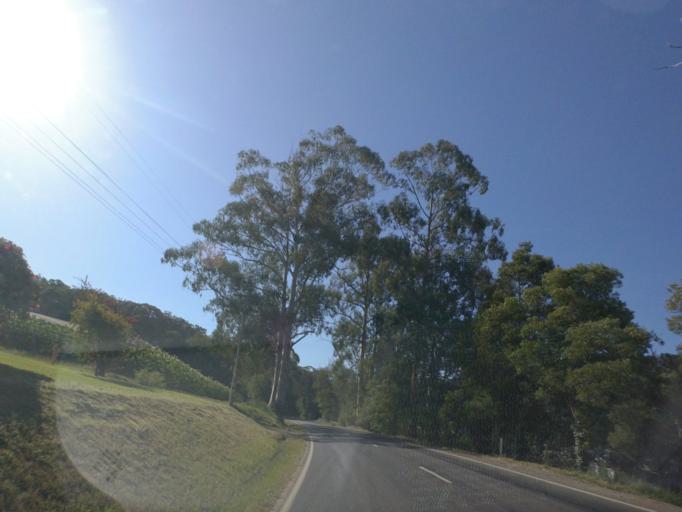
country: AU
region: Victoria
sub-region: Yarra Ranges
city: Yarra Junction
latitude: -37.8398
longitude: 145.6793
